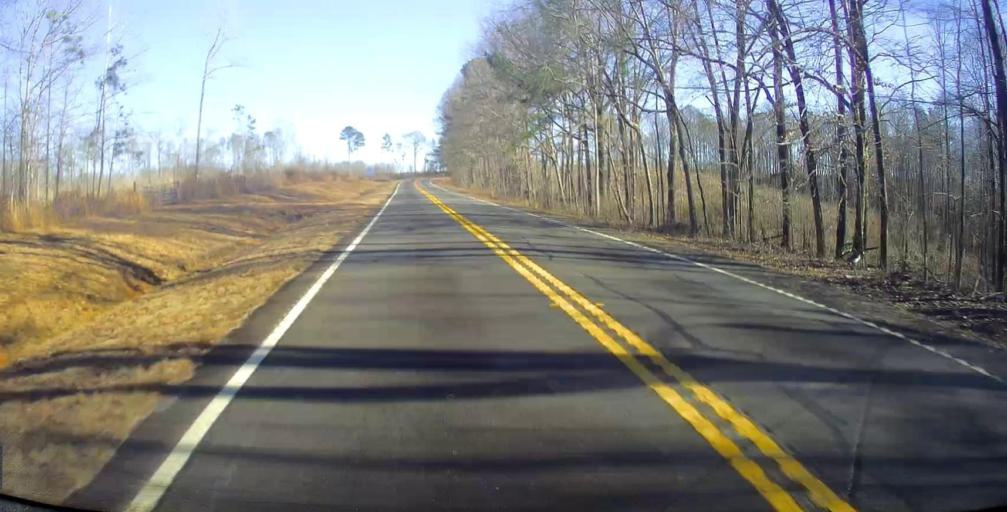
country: US
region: Georgia
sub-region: Talbot County
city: Talbotton
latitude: 32.6695
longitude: -84.4678
